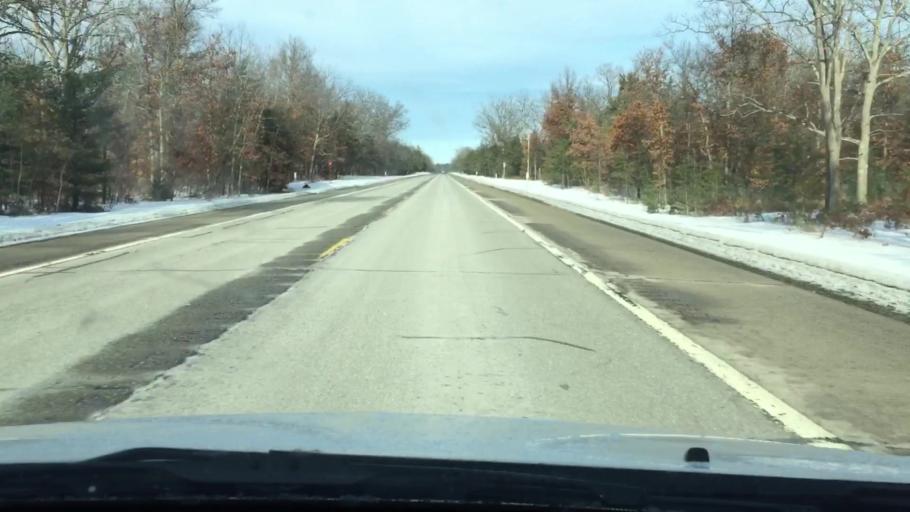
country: US
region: Michigan
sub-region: Wexford County
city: Manton
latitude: 44.5296
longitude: -85.3856
